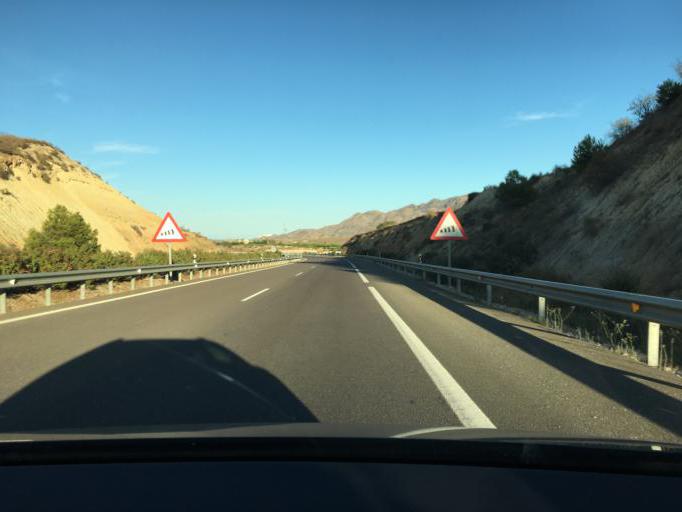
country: ES
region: Andalusia
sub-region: Provincia de Almeria
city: Bedar
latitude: 37.1455
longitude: -1.9679
